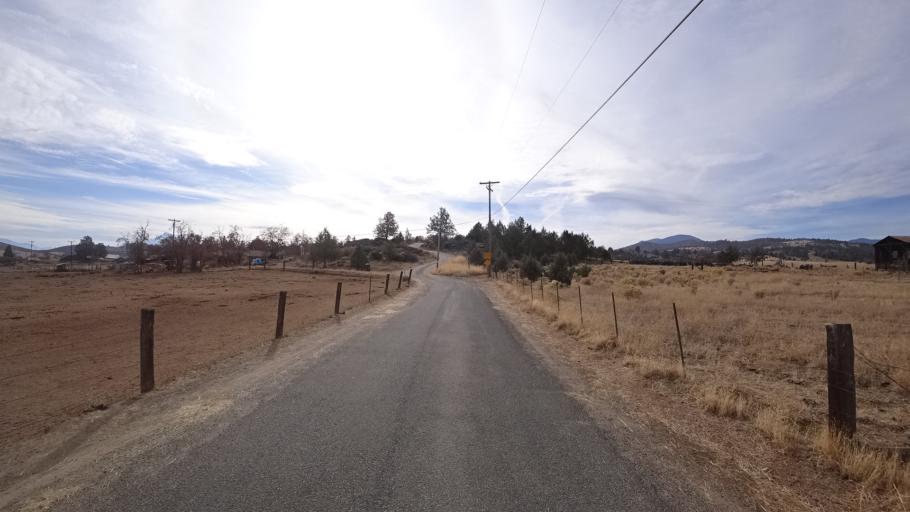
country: US
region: California
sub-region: Siskiyou County
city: Montague
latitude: 41.6944
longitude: -122.5639
